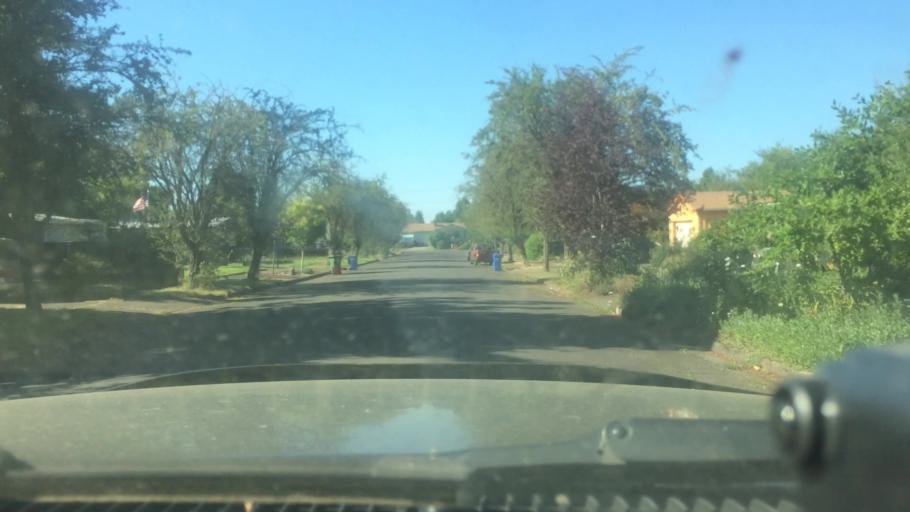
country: US
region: Oregon
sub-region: Lane County
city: Eugene
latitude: 44.0318
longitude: -123.1085
